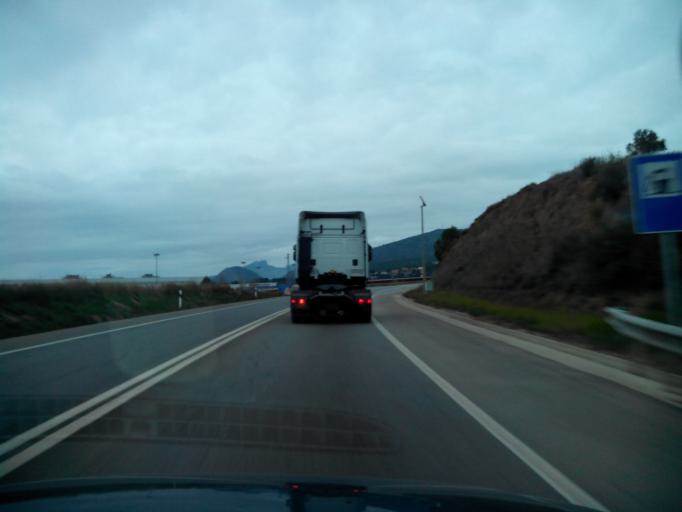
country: ES
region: Catalonia
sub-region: Provincia de Barcelona
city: Viladecavalls
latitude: 41.5605
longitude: 1.9703
